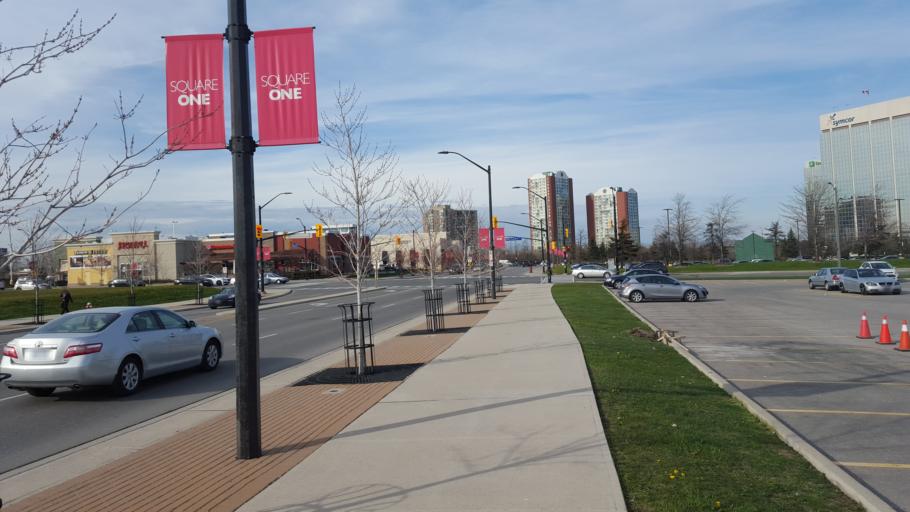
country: CA
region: Ontario
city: Mississauga
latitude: 43.5953
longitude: -79.6436
